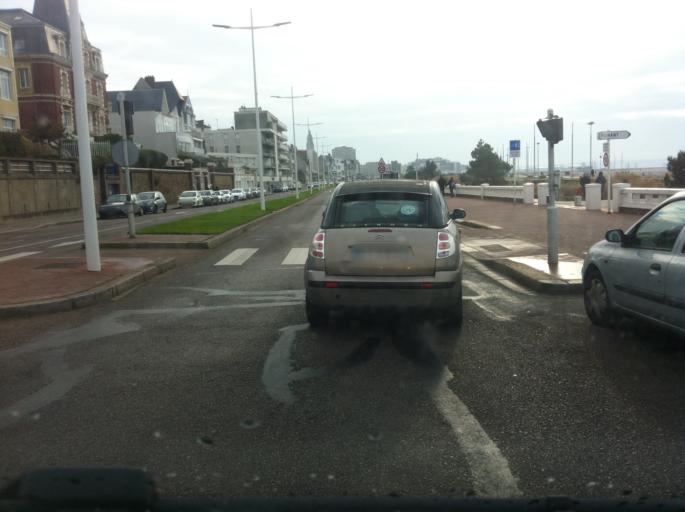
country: FR
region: Haute-Normandie
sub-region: Departement de la Seine-Maritime
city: Sainte-Adresse
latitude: 49.4998
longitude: 0.0897
